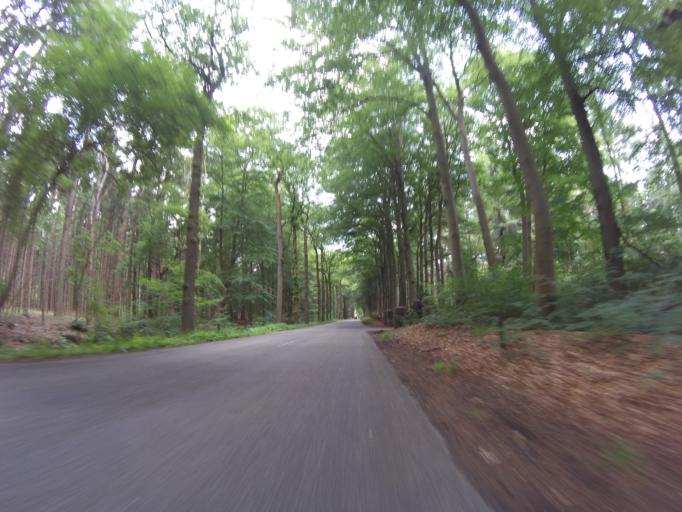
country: NL
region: Utrecht
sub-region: Gemeente Soest
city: Soest
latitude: 52.1659
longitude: 5.2269
